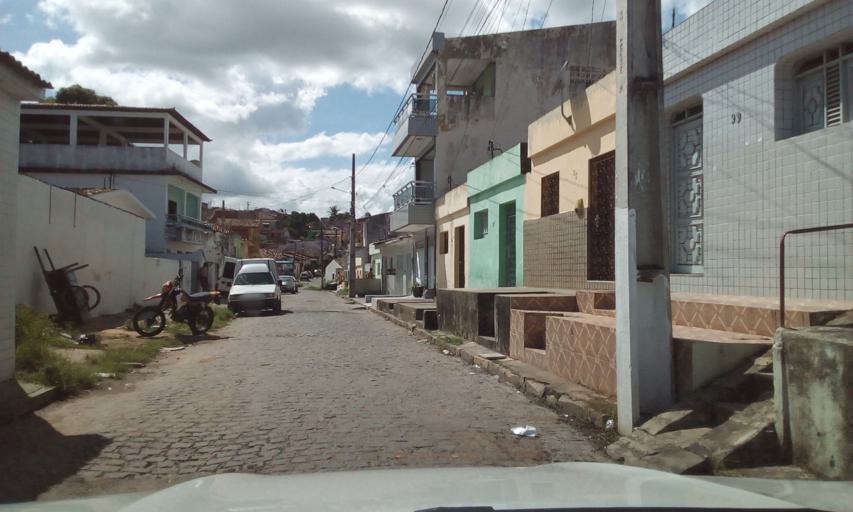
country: BR
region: Paraiba
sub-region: Guarabira
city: Guarabira
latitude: -6.8553
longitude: -35.4814
